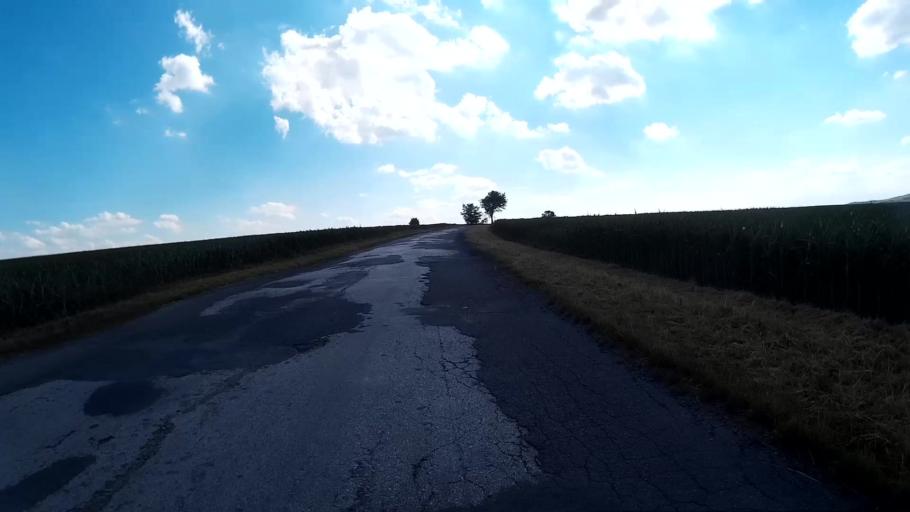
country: CZ
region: South Moravian
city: Krepice
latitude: 49.0192
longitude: 16.7056
